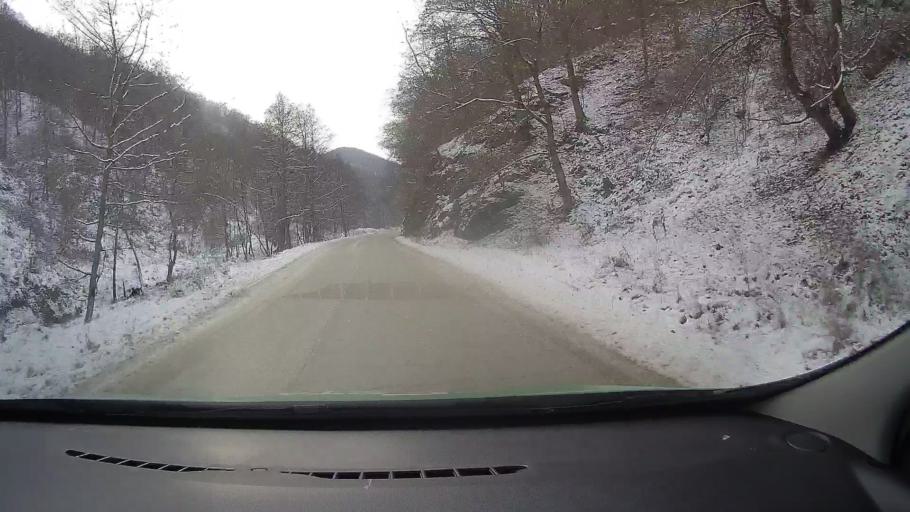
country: RO
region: Alba
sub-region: Oras Zlatna
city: Zlatna
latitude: 46.1045
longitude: 23.1924
